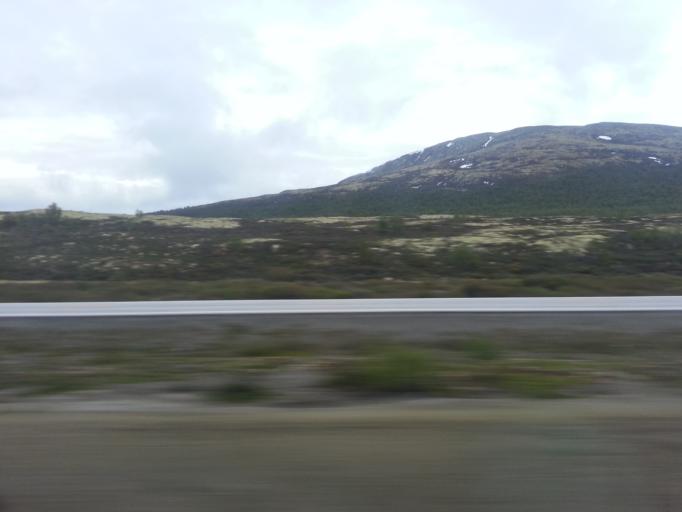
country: NO
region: Sor-Trondelag
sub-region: Oppdal
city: Oppdal
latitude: 62.2598
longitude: 9.5564
